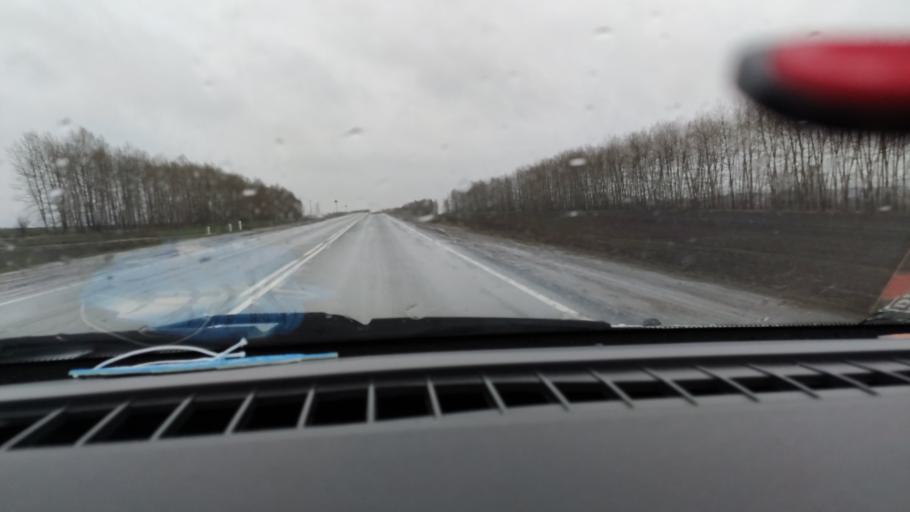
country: RU
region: Tatarstan
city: Mendeleyevsk
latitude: 55.9264
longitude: 52.2780
